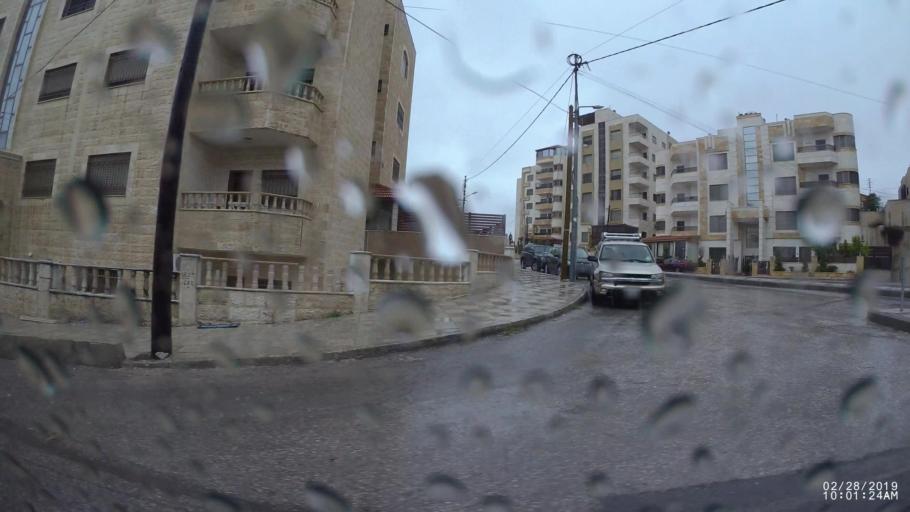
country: JO
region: Amman
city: Al Jubayhah
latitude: 32.0168
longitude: 35.8843
